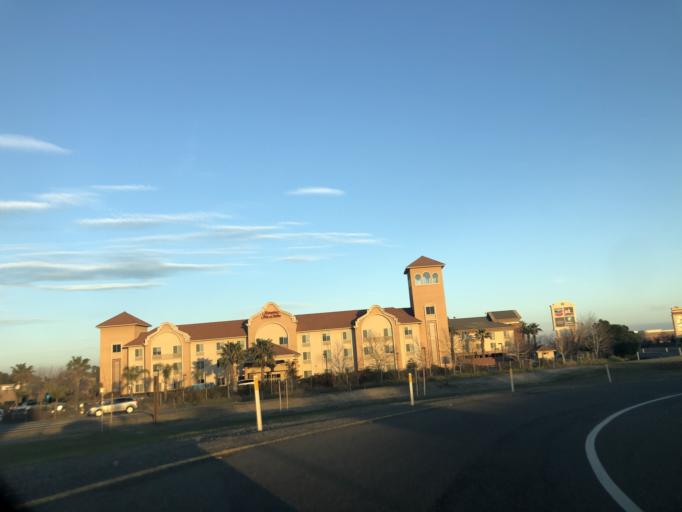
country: US
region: California
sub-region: Yolo County
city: Woodland
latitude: 38.6748
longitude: -121.7279
